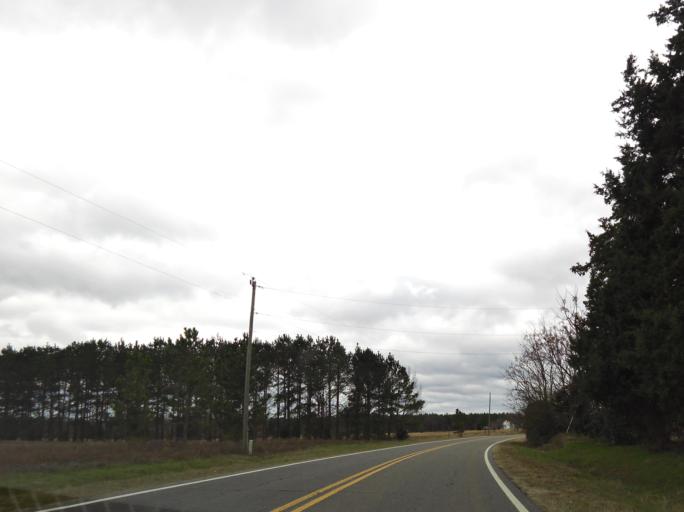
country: US
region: Georgia
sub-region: Bleckley County
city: Cochran
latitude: 32.4871
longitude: -83.3713
